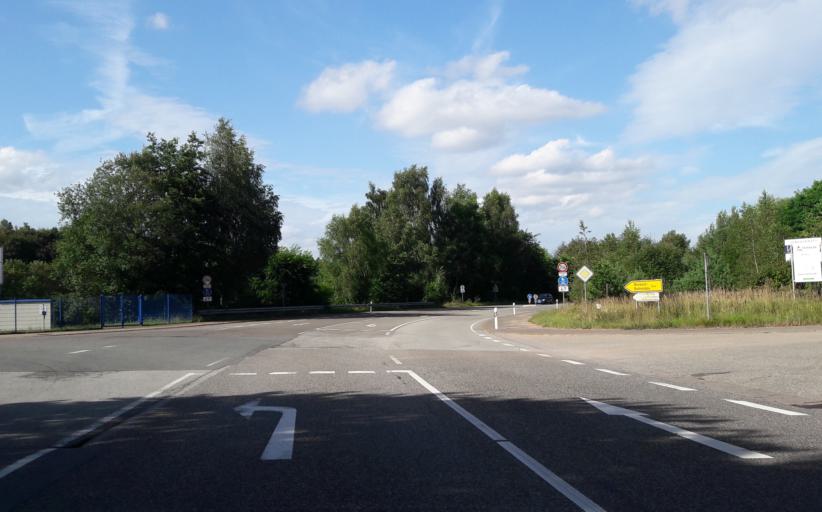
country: DE
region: Saarland
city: Bexbach
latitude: 49.3388
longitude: 7.2404
